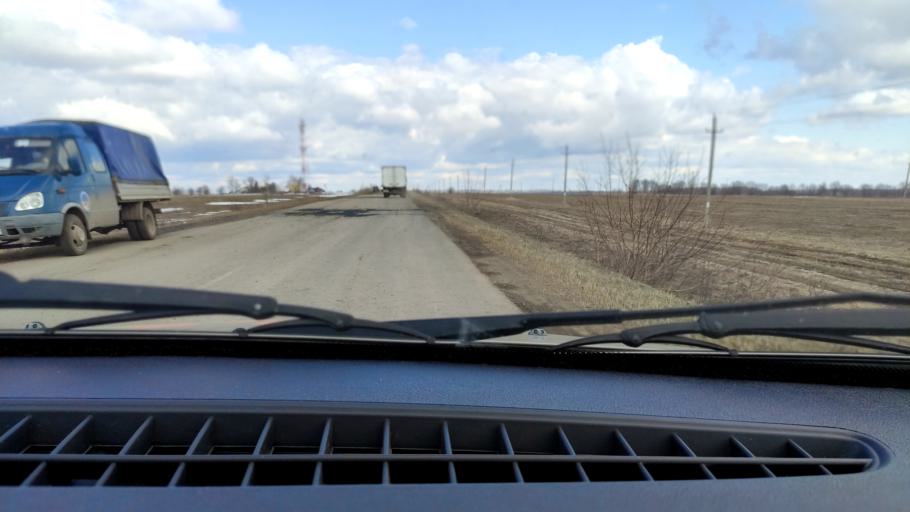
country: RU
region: Bashkortostan
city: Kudeyevskiy
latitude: 54.8381
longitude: 56.7940
